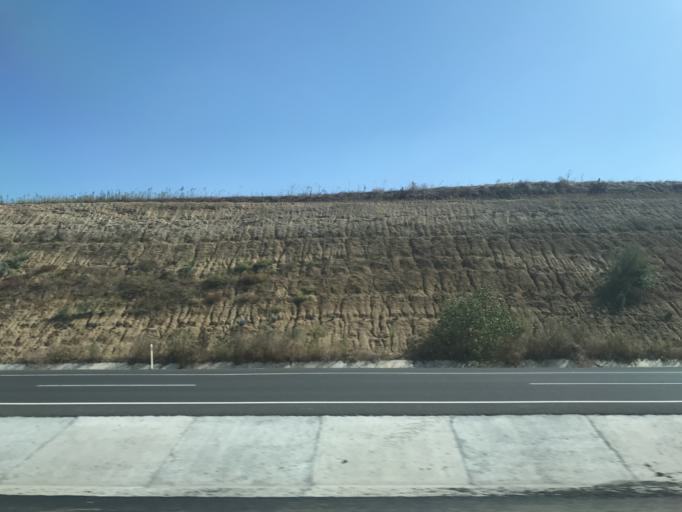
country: TR
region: Tekirdag
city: Muratli
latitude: 41.1509
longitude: 27.4970
